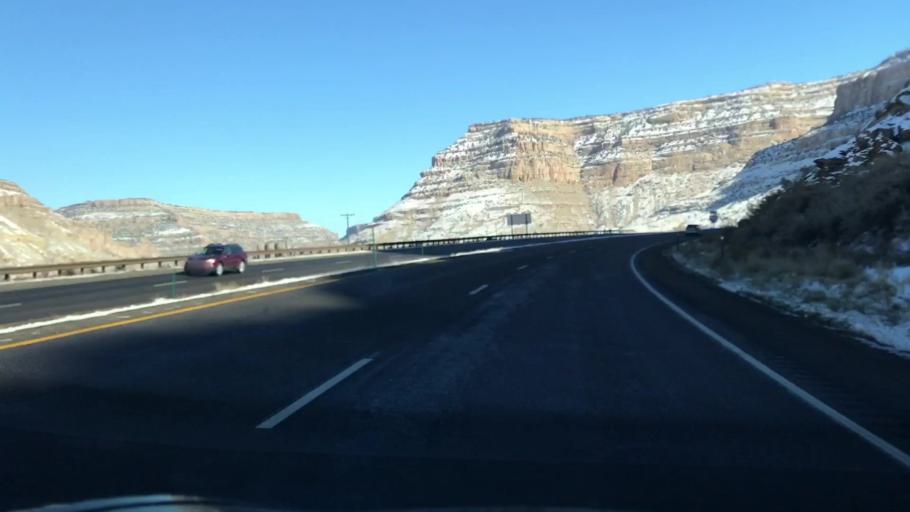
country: US
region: Colorado
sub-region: Mesa County
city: Palisade
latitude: 39.1477
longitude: -108.3127
